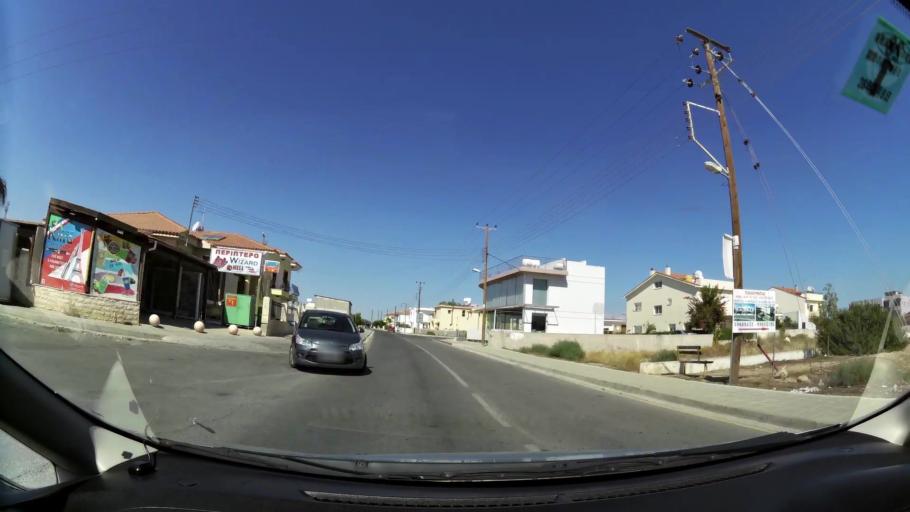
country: CY
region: Larnaka
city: Livadia
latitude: 34.9593
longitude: 33.6349
